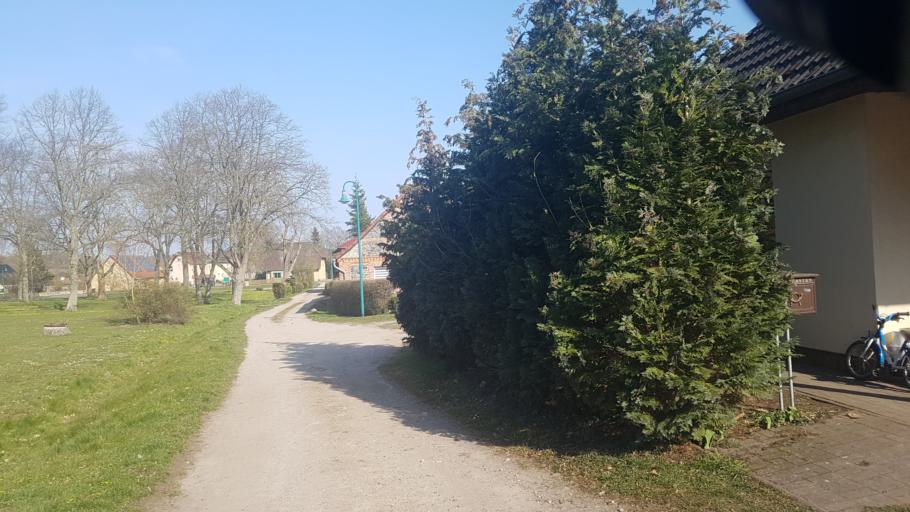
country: DE
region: Brandenburg
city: Prenzlau
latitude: 53.2277
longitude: 13.8405
